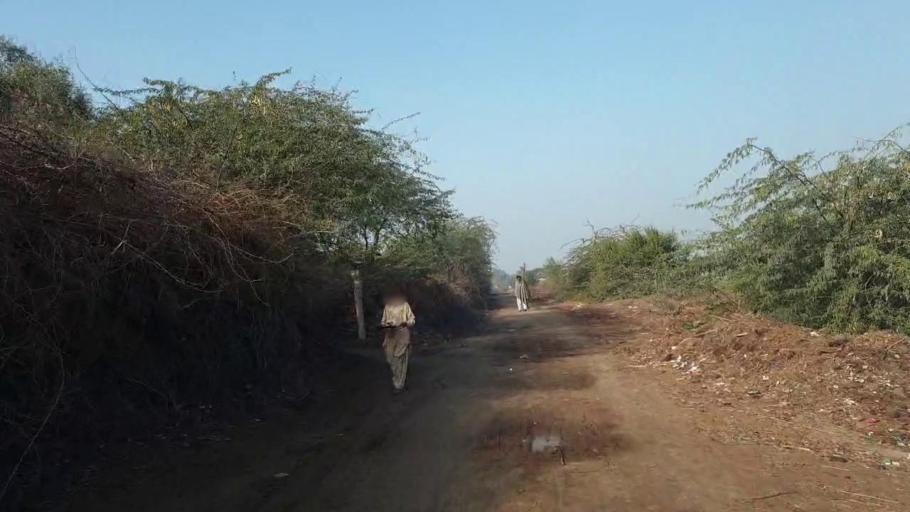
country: PK
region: Sindh
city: Shahdadpur
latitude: 25.9722
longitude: 68.6122
